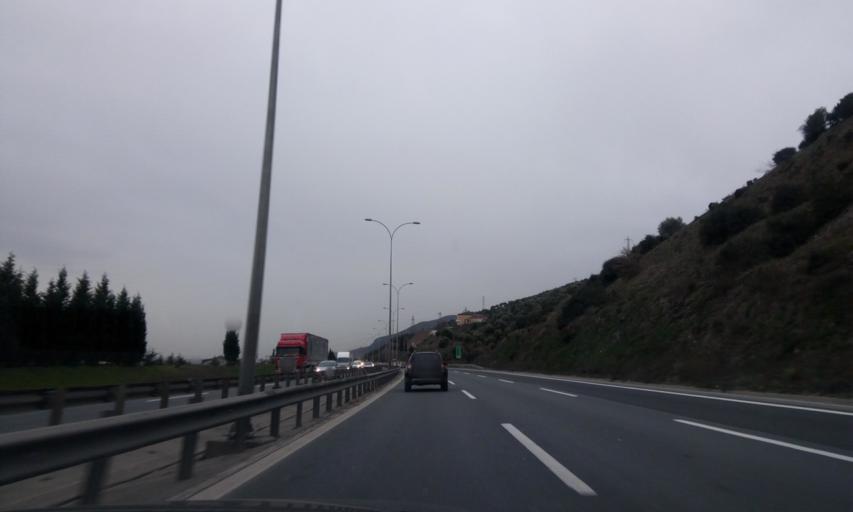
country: TR
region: Kocaeli
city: Korfez
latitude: 40.7790
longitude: 29.7152
